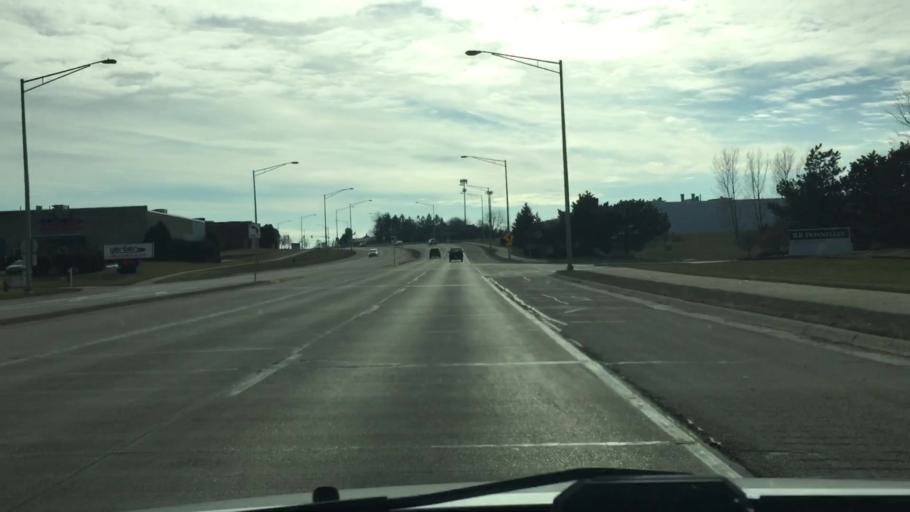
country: US
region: Illinois
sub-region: Kane County
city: Saint Charles
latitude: 41.9116
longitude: -88.2774
